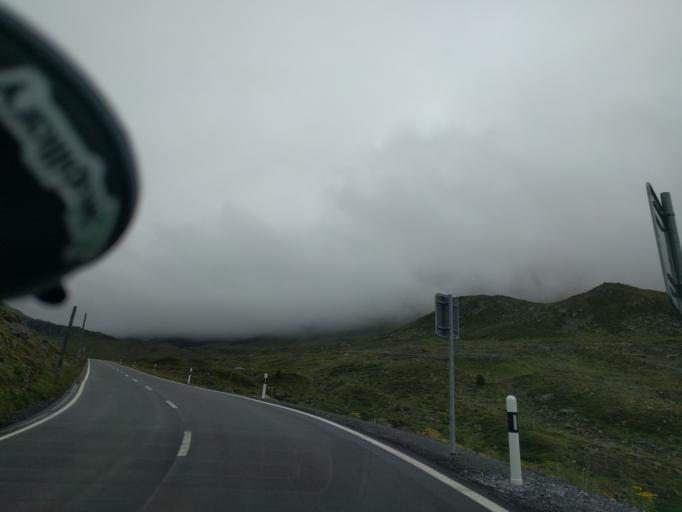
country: CH
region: Grisons
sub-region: Praettigau/Davos District
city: Davos
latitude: 46.7676
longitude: 9.9411
